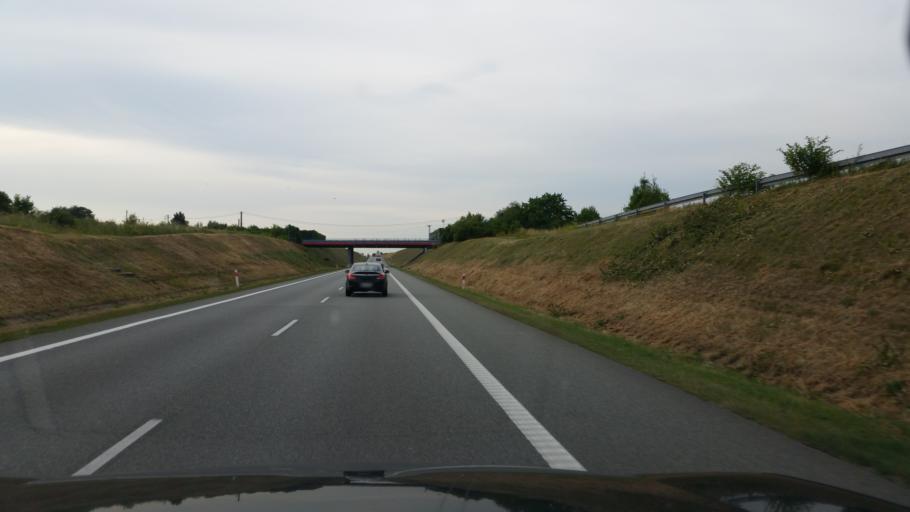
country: PL
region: Silesian Voivodeship
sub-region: Powiat bedzinski
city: Mierzecice
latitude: 50.4362
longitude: 19.1490
